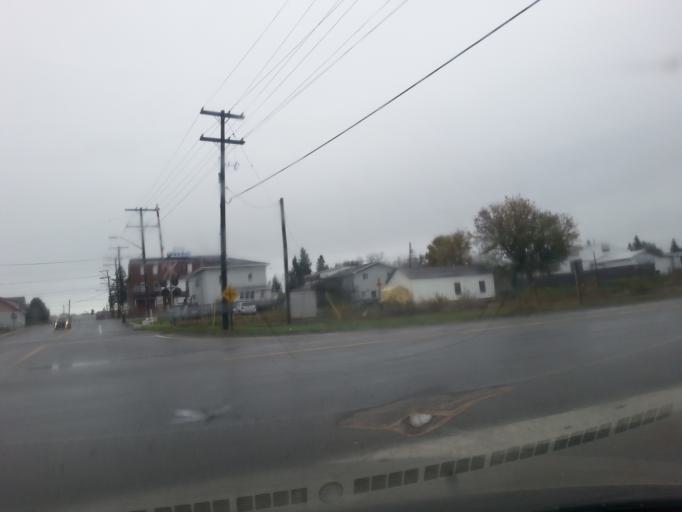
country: CA
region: Ontario
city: Greater Sudbury
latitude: 46.4419
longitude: -80.3109
